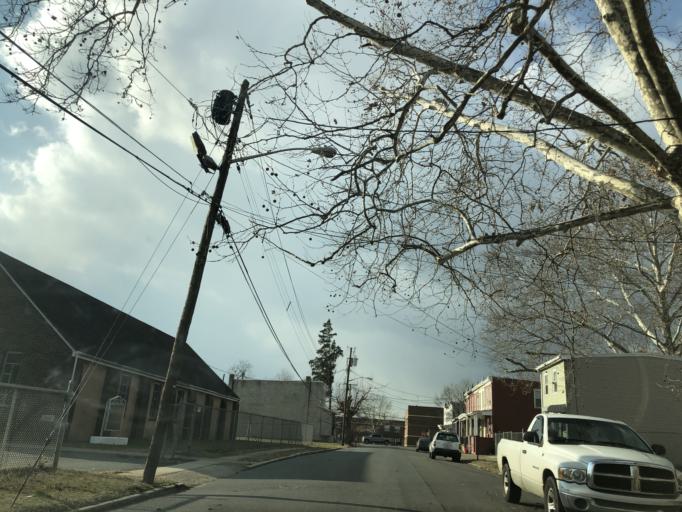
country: US
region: New Jersey
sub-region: Camden County
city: Wood-Lynne
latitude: 39.9162
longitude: -75.1091
